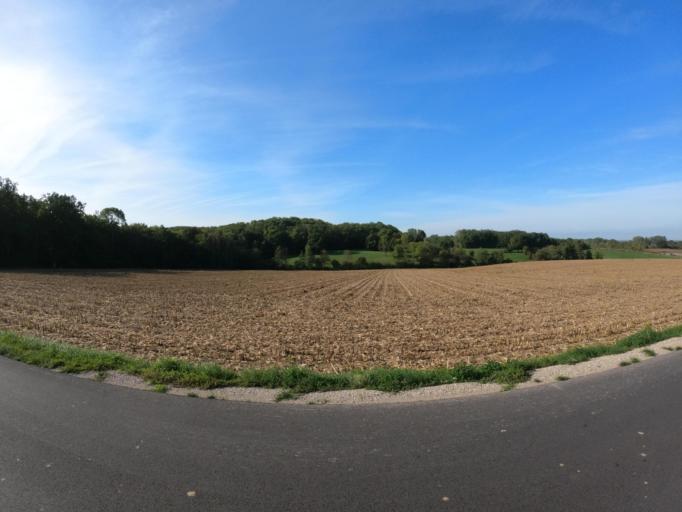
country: FR
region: Franche-Comte
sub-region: Departement du Jura
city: Montmorot
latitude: 46.7248
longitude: 5.5111
